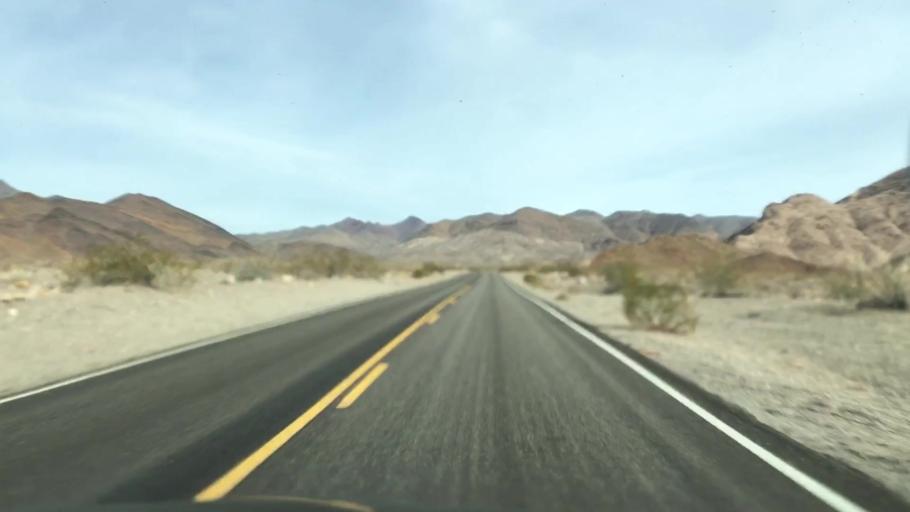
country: US
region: Nevada
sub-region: Nye County
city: Beatty
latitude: 36.7191
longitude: -116.9796
